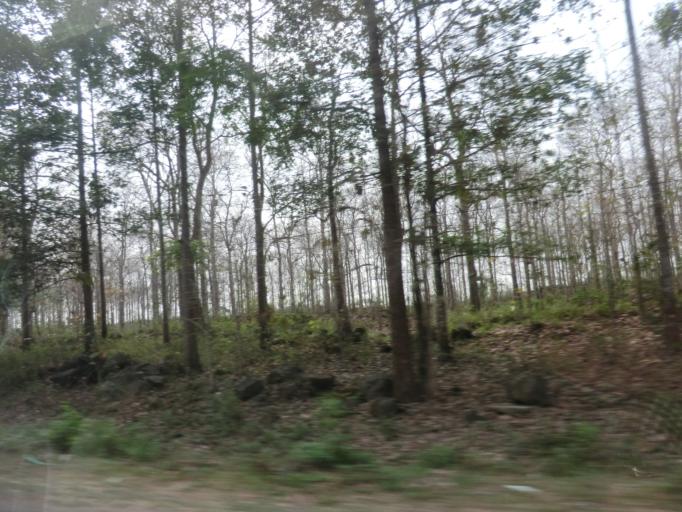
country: VN
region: Dong Nai
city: Tan Phu
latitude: 11.2533
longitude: 107.4099
